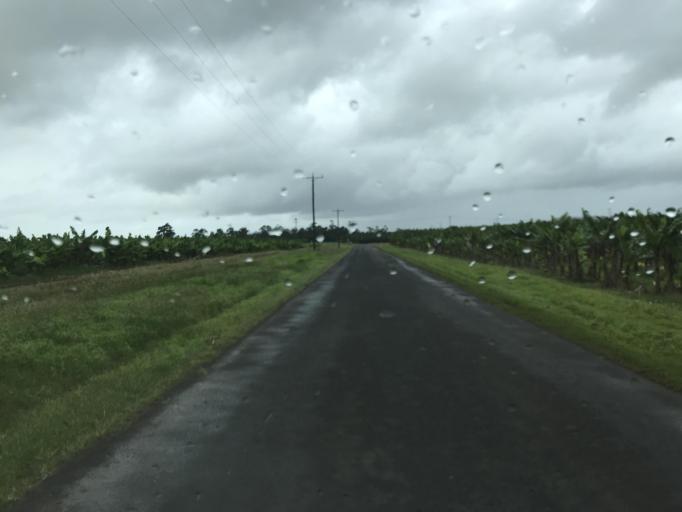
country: AU
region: Queensland
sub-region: Cassowary Coast
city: Innisfail
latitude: -17.5134
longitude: 145.9789
